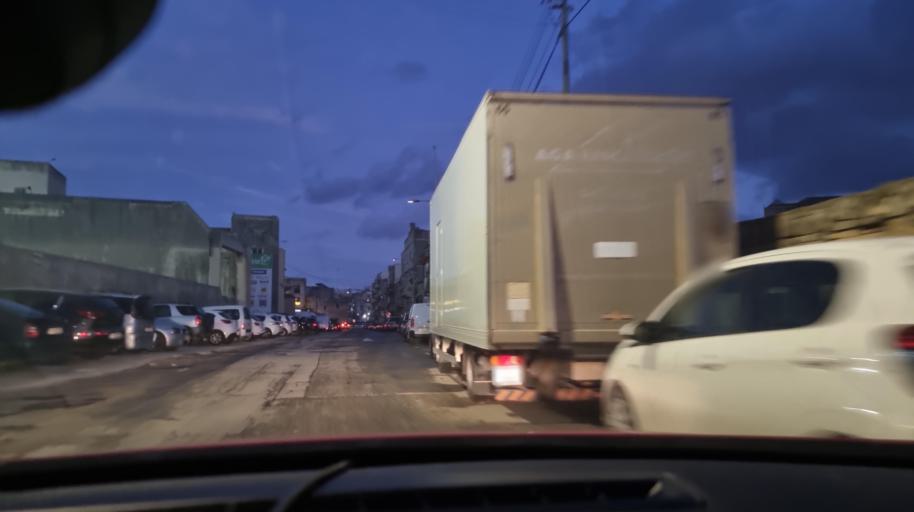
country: MT
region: Qormi
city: Qormi
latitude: 35.8822
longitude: 14.4763
